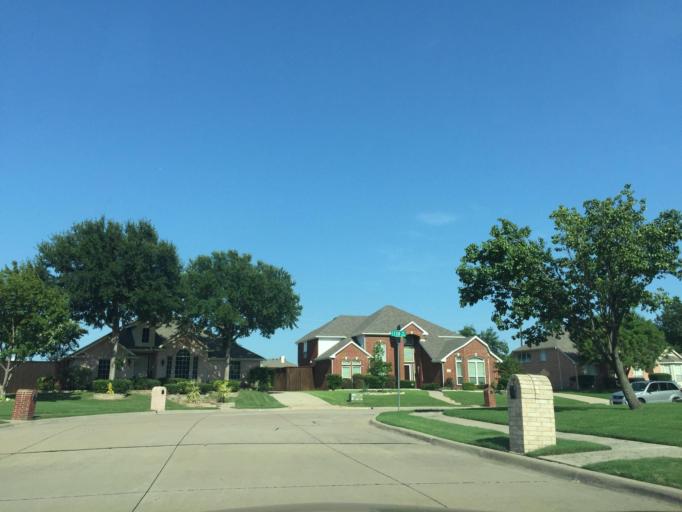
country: US
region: Texas
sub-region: Denton County
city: Lewisville
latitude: 33.0147
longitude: -96.9330
